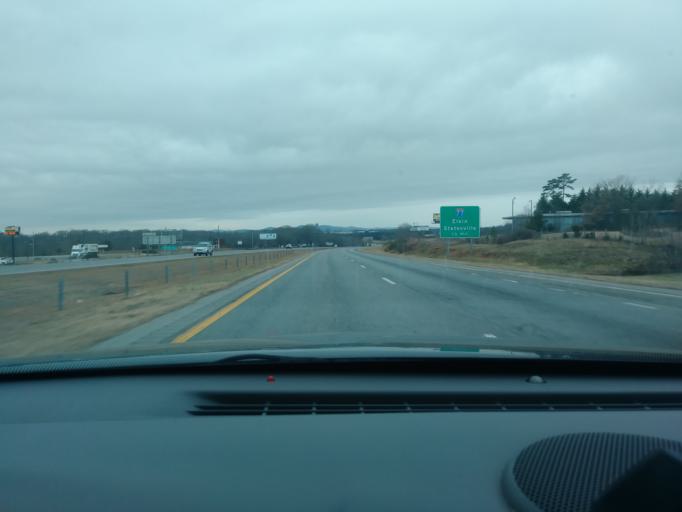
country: US
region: North Carolina
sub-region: Yadkin County
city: Jonesville
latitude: 36.1195
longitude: -80.8006
